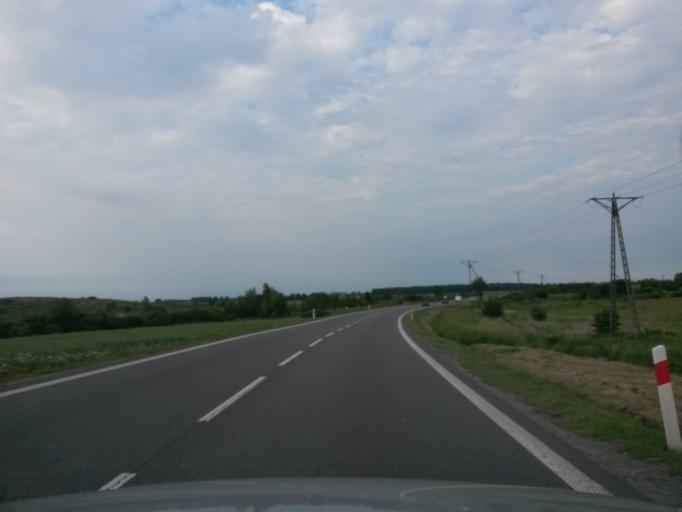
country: PL
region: Lower Silesian Voivodeship
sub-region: Powiat sredzki
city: Udanin
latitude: 50.9960
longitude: 16.4544
